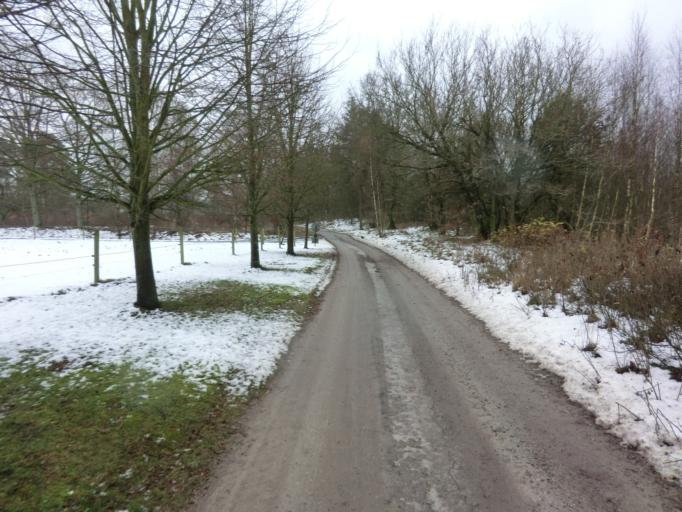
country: SE
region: Skane
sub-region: Hoors Kommun
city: Loberod
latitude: 55.7395
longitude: 13.3977
